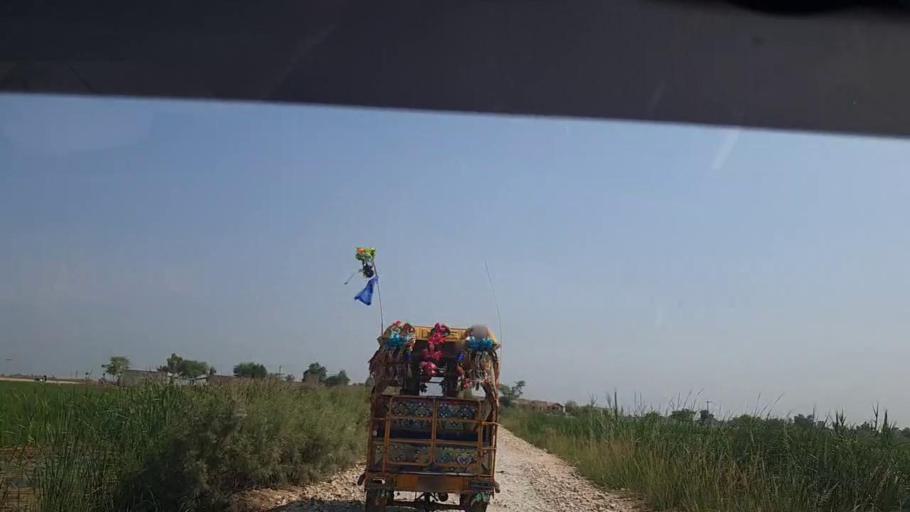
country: PK
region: Sindh
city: Thul
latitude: 28.1951
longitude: 68.7336
